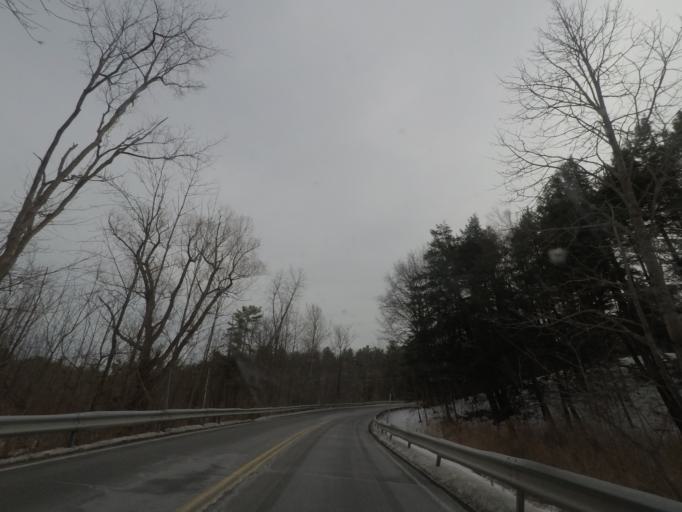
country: US
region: New York
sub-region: Albany County
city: Voorheesville
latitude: 42.6622
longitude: -73.9843
